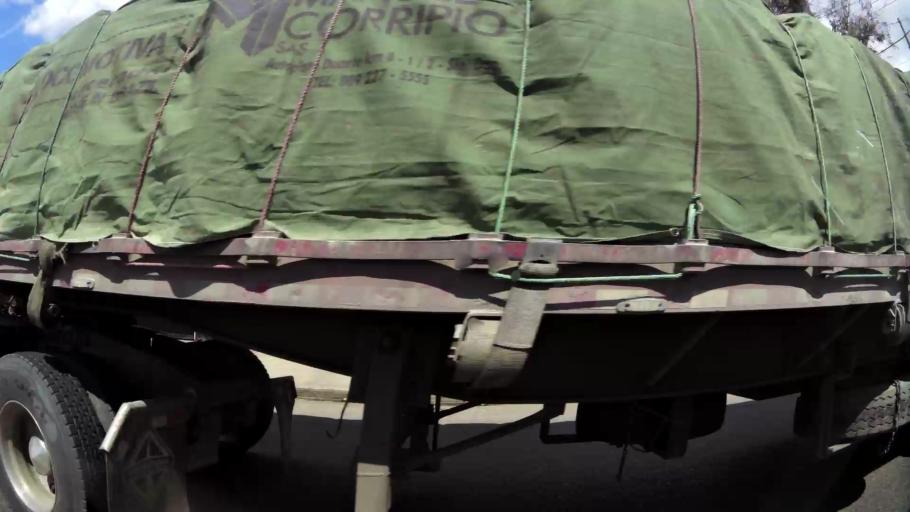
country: DO
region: Santiago
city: Santiago de los Caballeros
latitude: 19.4075
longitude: -70.6702
